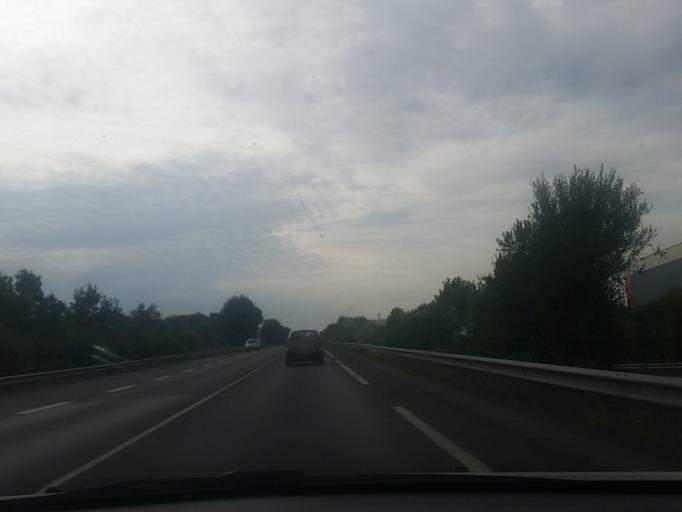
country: FR
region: Pays de la Loire
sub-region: Departement de la Vendee
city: Saint-Fulgent
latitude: 46.8606
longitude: -1.1731
